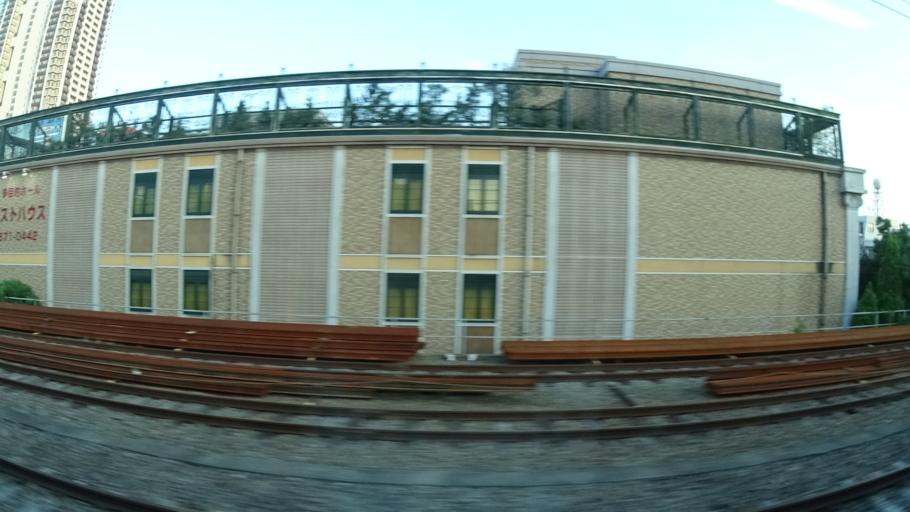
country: JP
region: Chiba
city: Matsudo
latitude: 35.7691
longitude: 139.8696
